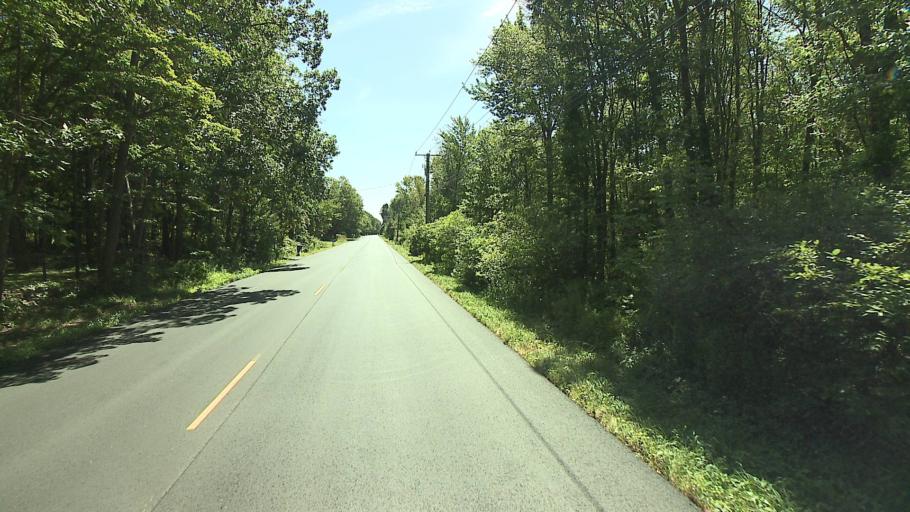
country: US
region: Connecticut
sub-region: Litchfield County
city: New Hartford Center
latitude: 41.9290
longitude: -72.9143
